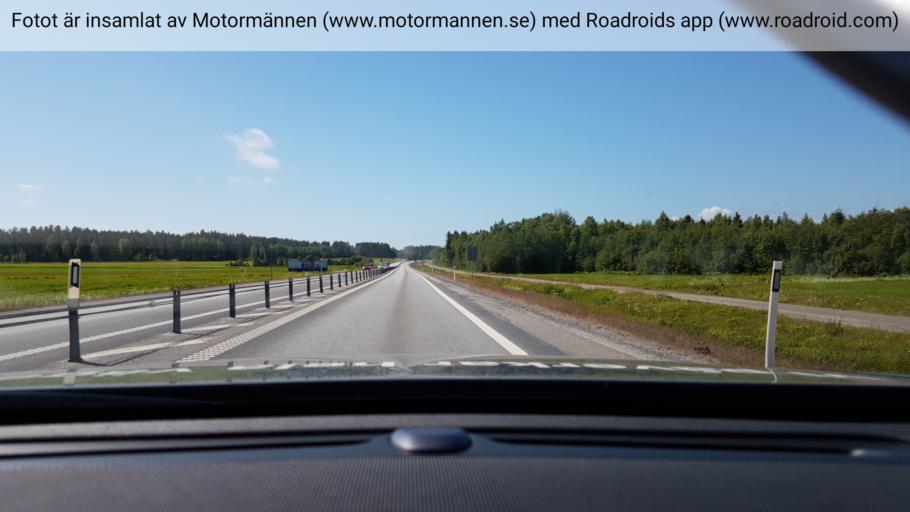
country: SE
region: Vaesterbotten
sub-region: Umea Kommun
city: Roback
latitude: 63.7651
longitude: 20.1732
